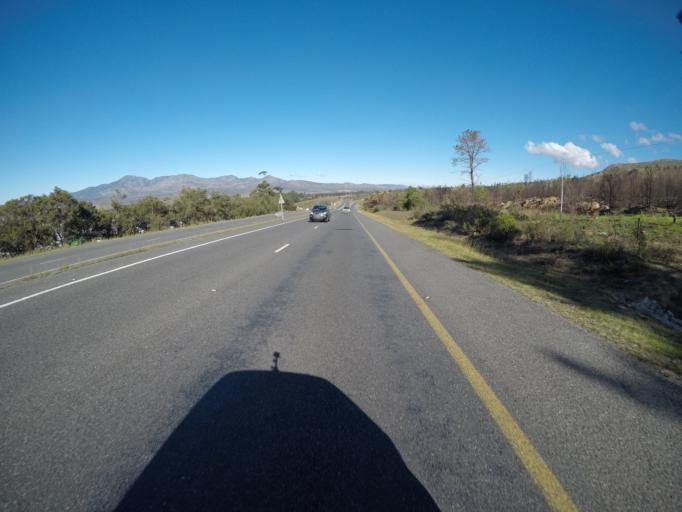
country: ZA
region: Western Cape
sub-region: Overberg District Municipality
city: Grabouw
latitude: -34.2237
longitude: 19.1877
